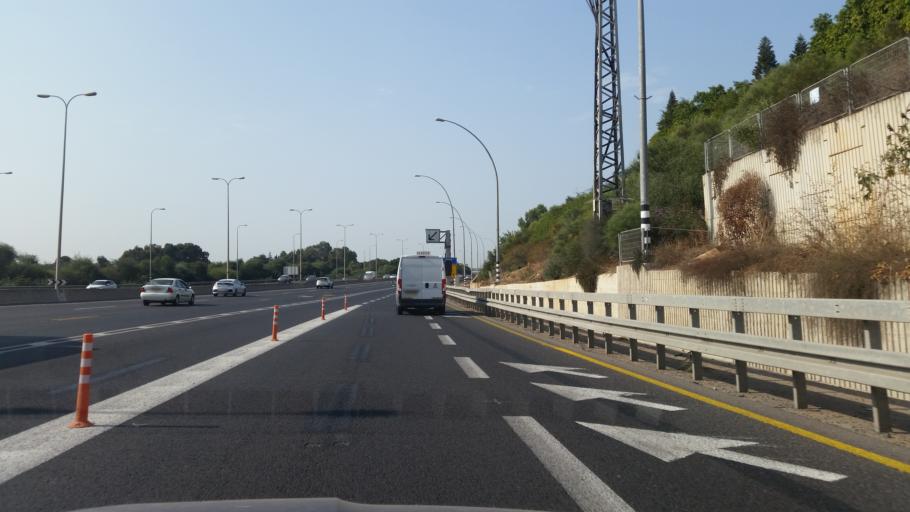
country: IL
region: Central District
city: Even Yehuda
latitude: 32.2713
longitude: 34.8512
